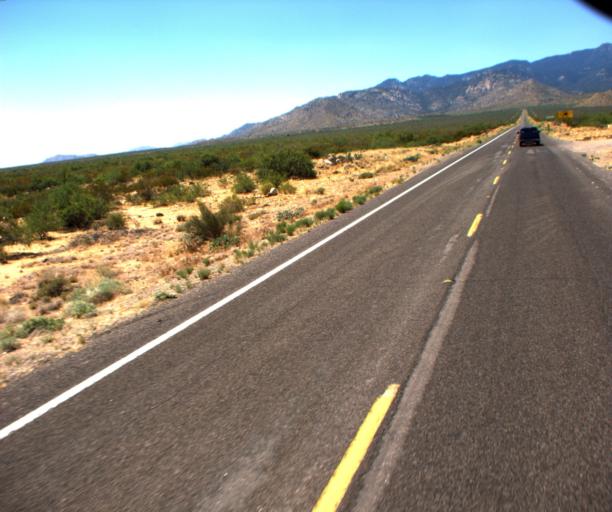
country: US
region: Arizona
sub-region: Graham County
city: Swift Trail Junction
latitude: 32.7140
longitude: -109.7302
